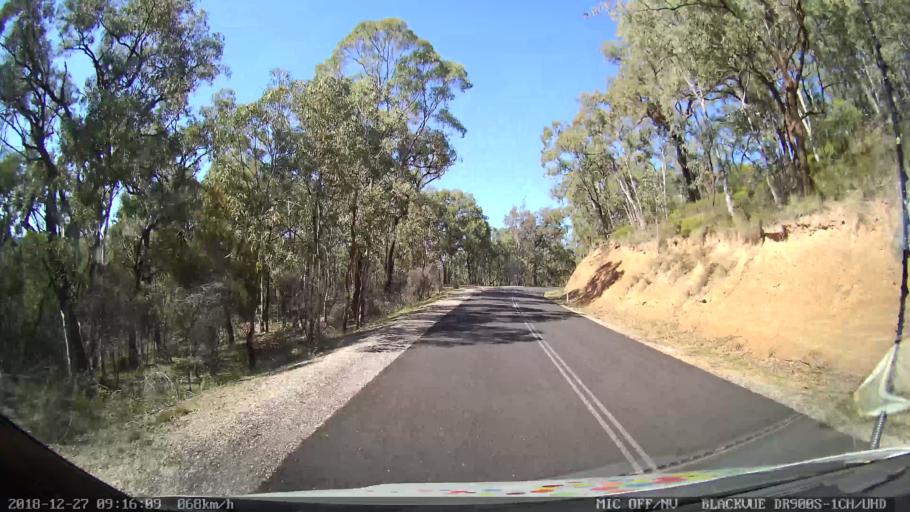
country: AU
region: New South Wales
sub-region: Lithgow
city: Portland
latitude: -33.1365
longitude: 150.0648
